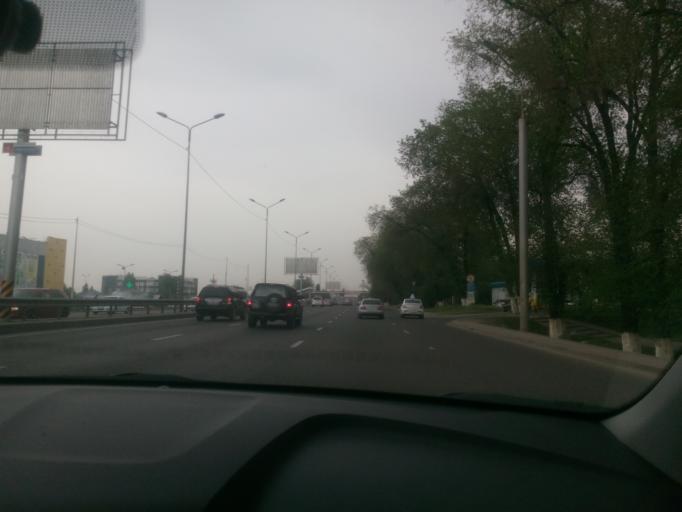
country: KZ
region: Almaty Qalasy
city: Almaty
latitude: 43.2411
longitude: 76.8178
